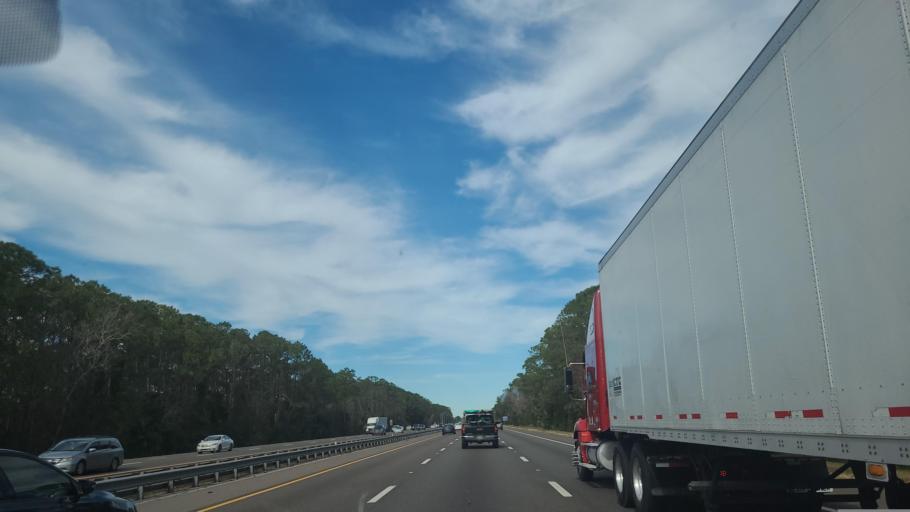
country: US
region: Florida
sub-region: Flagler County
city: Flagler Beach
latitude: 29.4627
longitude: -81.1779
